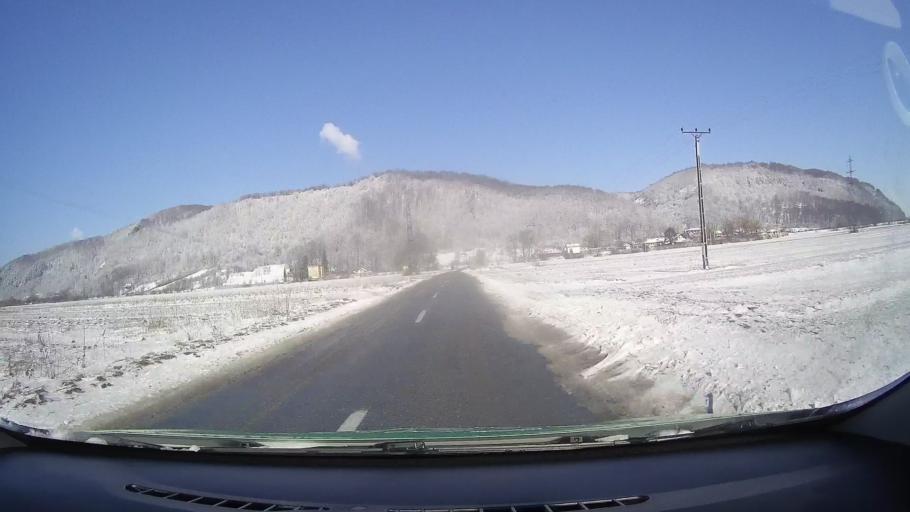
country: RO
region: Sibiu
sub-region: Comuna Turnu Rosu
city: Turnu Rosu
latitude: 45.6580
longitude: 24.2970
